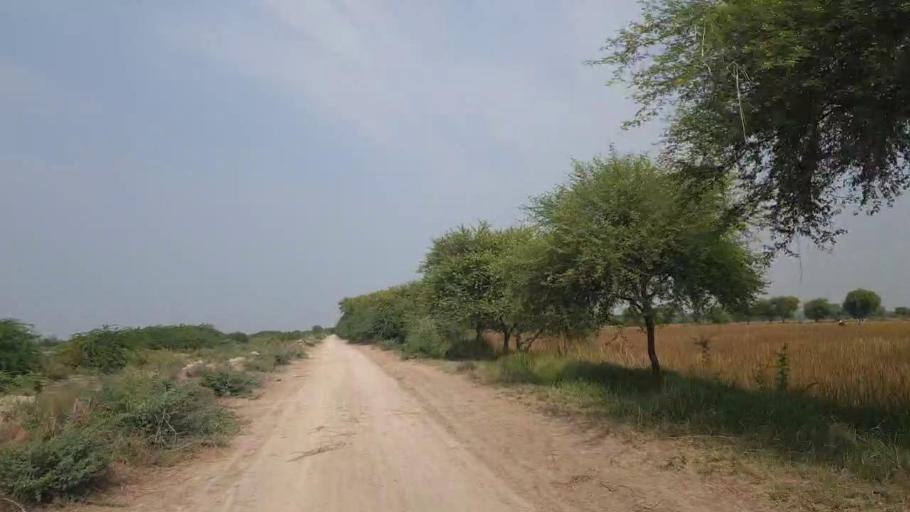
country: PK
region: Sindh
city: Badin
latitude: 24.5612
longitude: 68.7331
